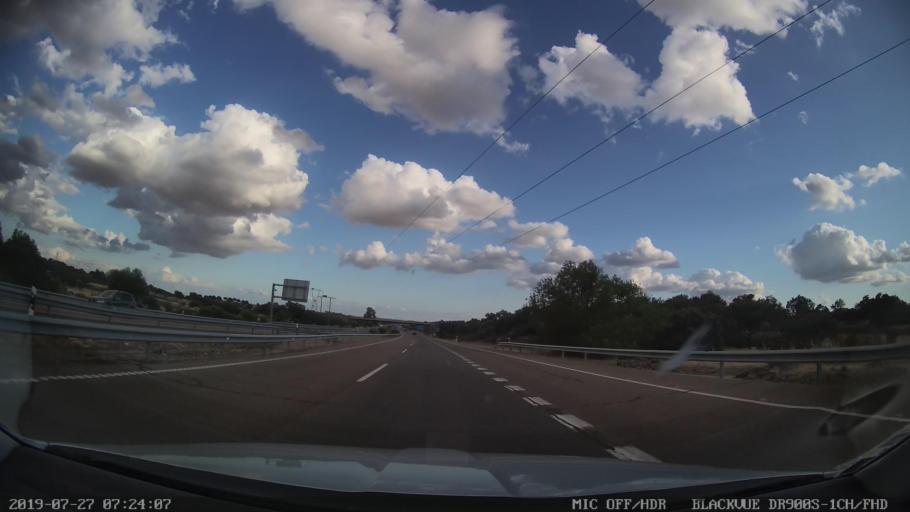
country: ES
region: Extremadura
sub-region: Provincia de Caceres
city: Puerto de Santa Cruz
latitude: 39.3048
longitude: -5.8574
